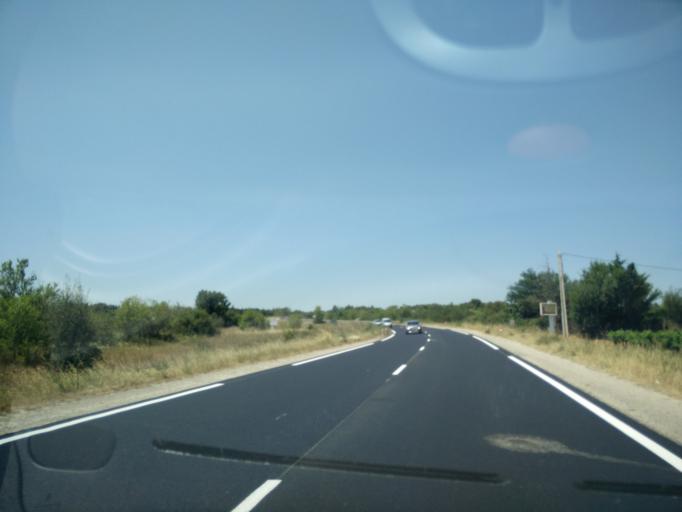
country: FR
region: Languedoc-Roussillon
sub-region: Departement de l'Herault
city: Lunel
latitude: 43.6943
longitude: 4.1380
